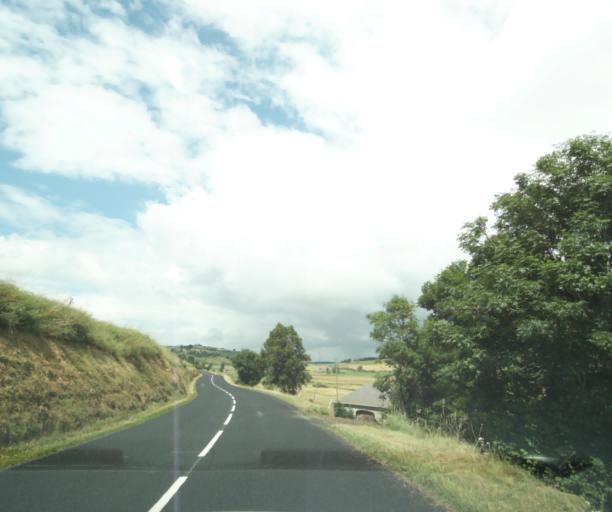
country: FR
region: Auvergne
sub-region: Departement de la Haute-Loire
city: Saugues
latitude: 44.8659
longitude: 3.4915
